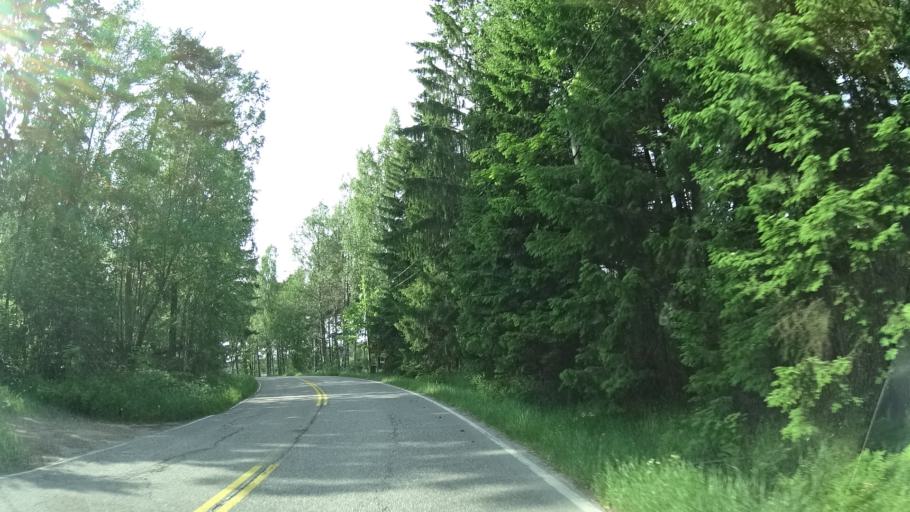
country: FI
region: Uusimaa
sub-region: Helsinki
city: Kirkkonummi
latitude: 60.0957
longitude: 24.5001
